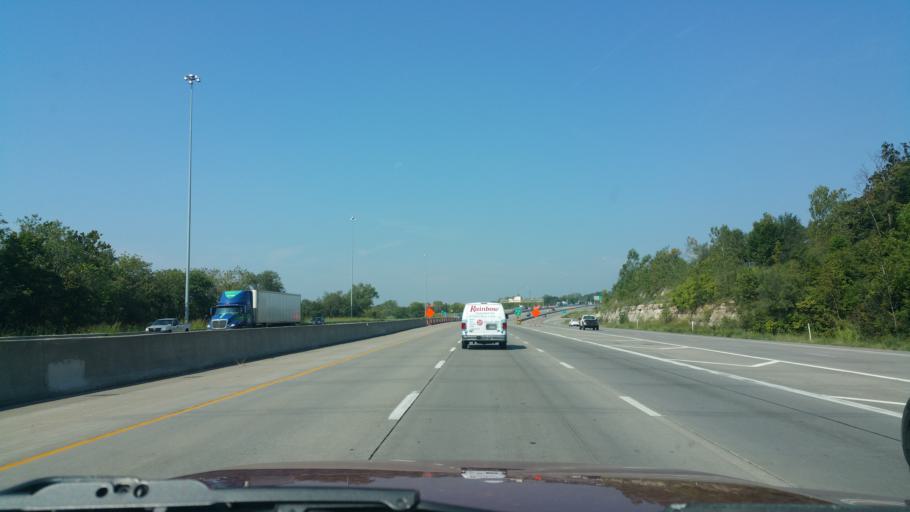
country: US
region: Kansas
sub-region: Wyandotte County
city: Kansas City
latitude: 39.0982
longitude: -94.6632
